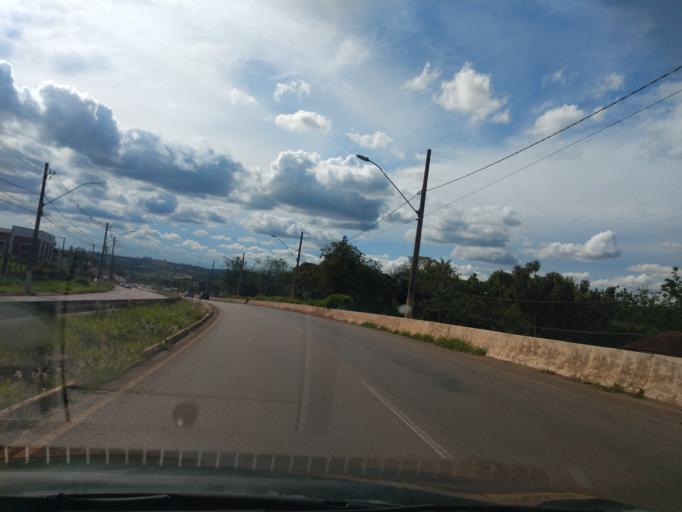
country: BR
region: Minas Gerais
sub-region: Tres Coracoes
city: Tres Coracoes
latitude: -21.6657
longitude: -45.2755
